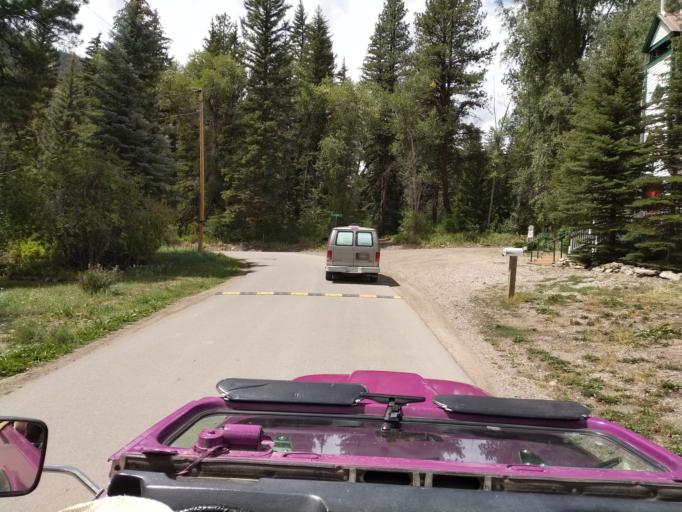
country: US
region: Colorado
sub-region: Gunnison County
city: Crested Butte
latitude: 39.0710
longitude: -107.1890
